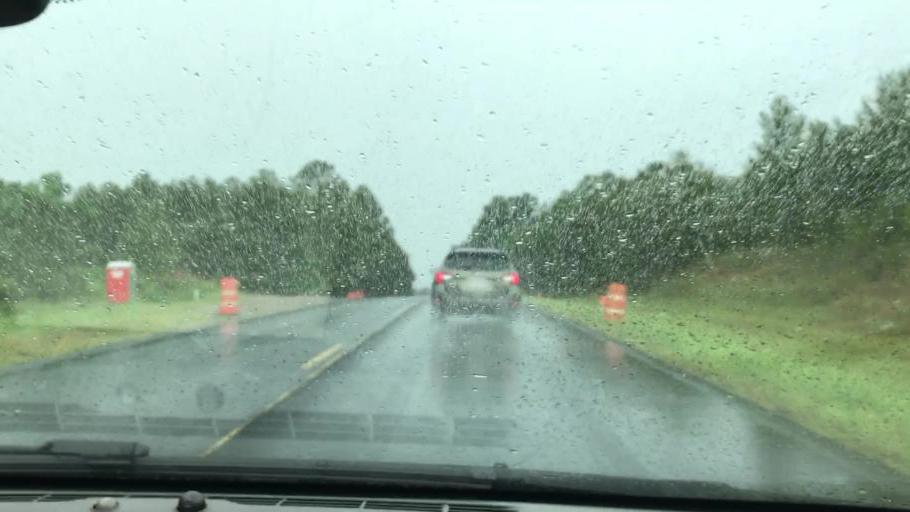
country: US
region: Georgia
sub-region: Clay County
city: Fort Gaines
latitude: 31.5892
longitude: -85.0314
